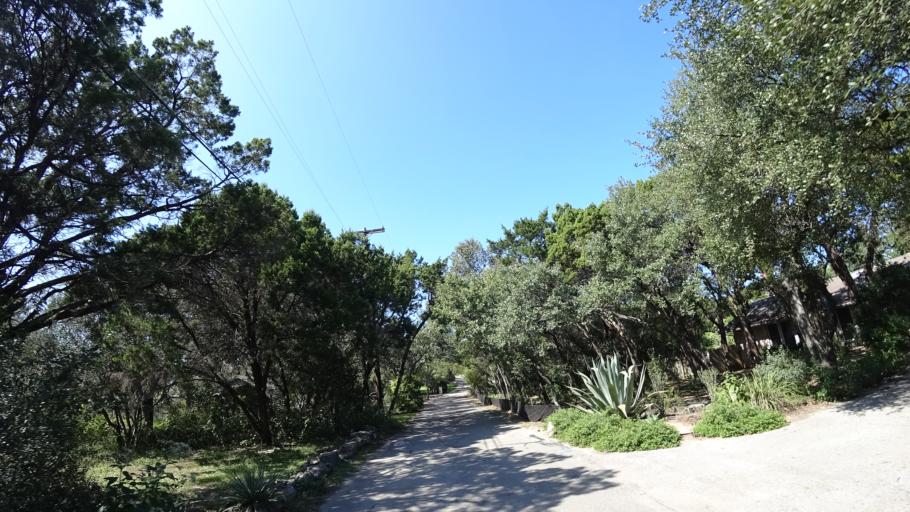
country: US
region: Texas
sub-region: Travis County
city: West Lake Hills
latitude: 30.2975
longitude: -97.8081
